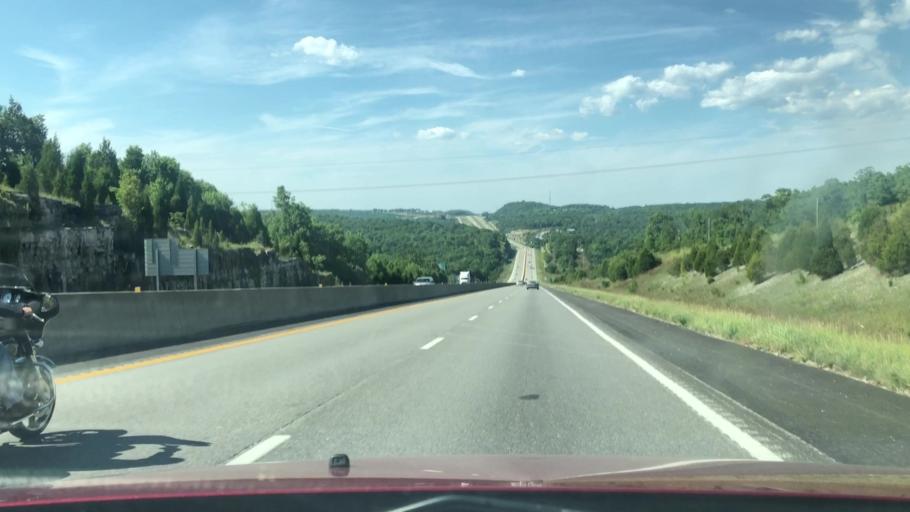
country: US
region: Missouri
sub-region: Taney County
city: Merriam Woods
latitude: 36.7192
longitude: -93.2207
